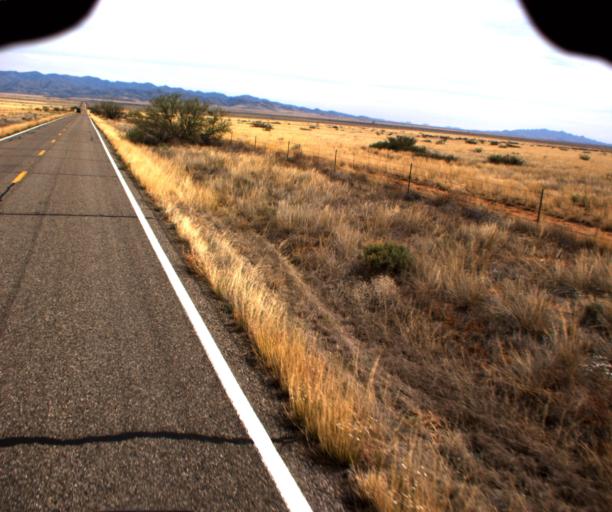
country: US
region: Arizona
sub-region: Cochise County
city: Willcox
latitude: 32.0876
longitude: -109.5283
